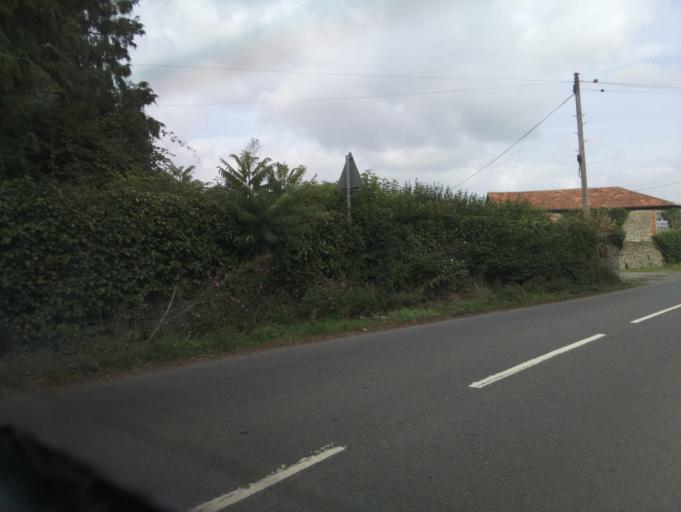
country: GB
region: England
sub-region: Dorset
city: Stalbridge
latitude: 50.9899
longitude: -2.4081
